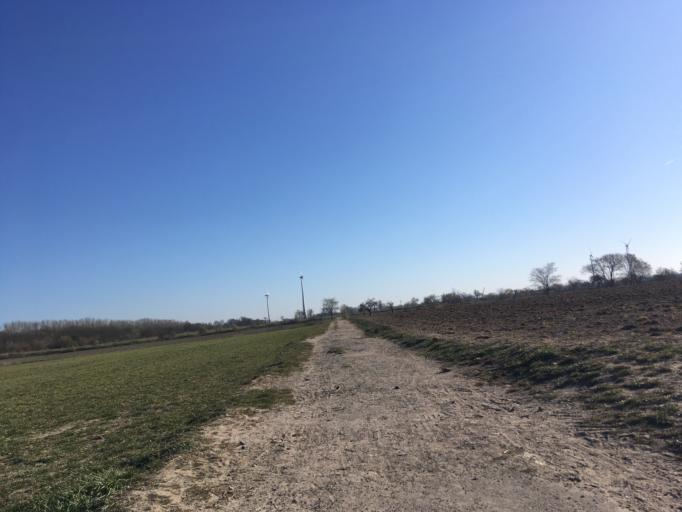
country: DE
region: Berlin
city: Blankenfelde
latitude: 52.6255
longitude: 13.4106
